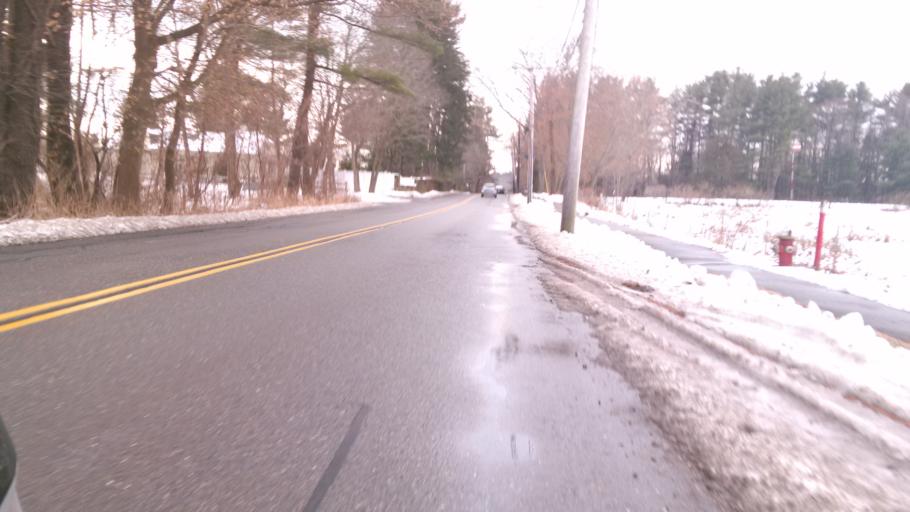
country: US
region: Massachusetts
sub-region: Middlesex County
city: Concord
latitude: 42.4451
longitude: -71.3631
